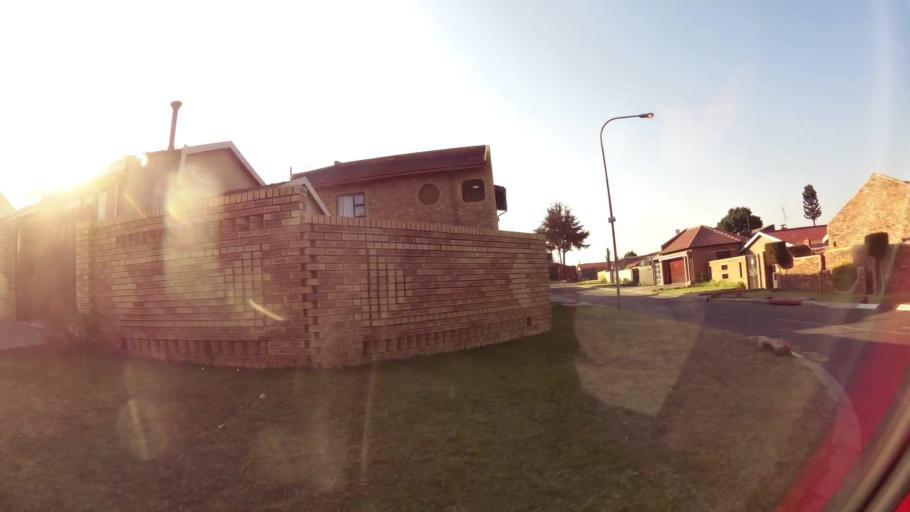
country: ZA
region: Gauteng
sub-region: City of Johannesburg Metropolitan Municipality
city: Soweto
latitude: -26.2532
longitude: 27.9537
